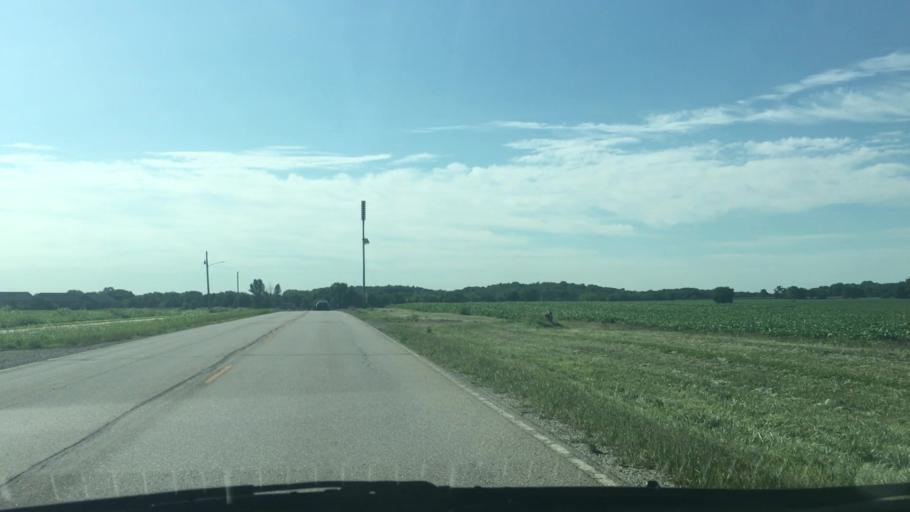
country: US
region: Iowa
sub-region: Johnson County
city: North Liberty
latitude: 41.7389
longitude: -91.5859
